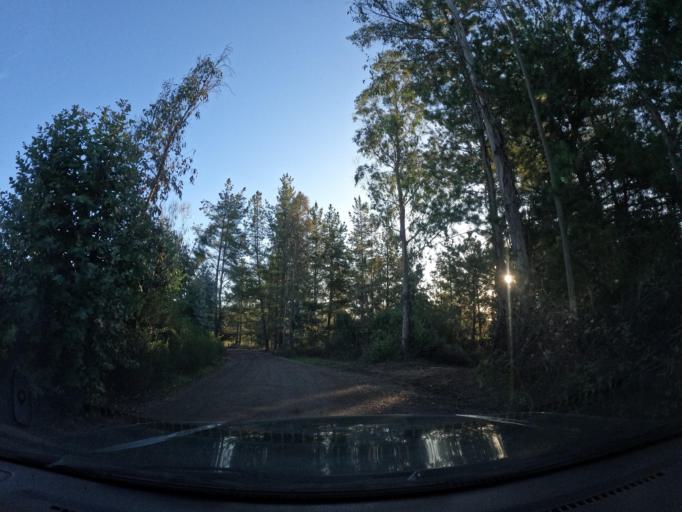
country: CL
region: Biobio
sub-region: Provincia de Concepcion
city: Chiguayante
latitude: -37.0130
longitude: -72.8465
